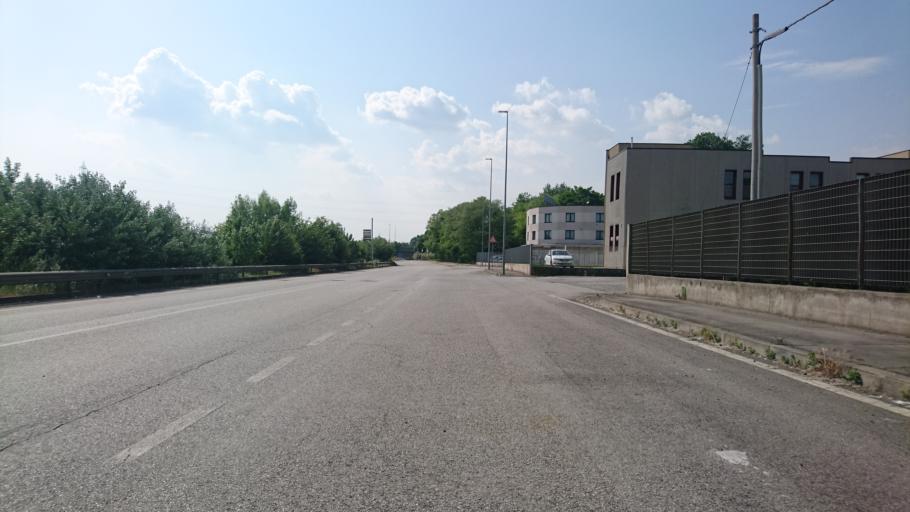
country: IT
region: Veneto
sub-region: Provincia di Padova
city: Ponte San Nicolo
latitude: 45.3817
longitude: 11.9425
